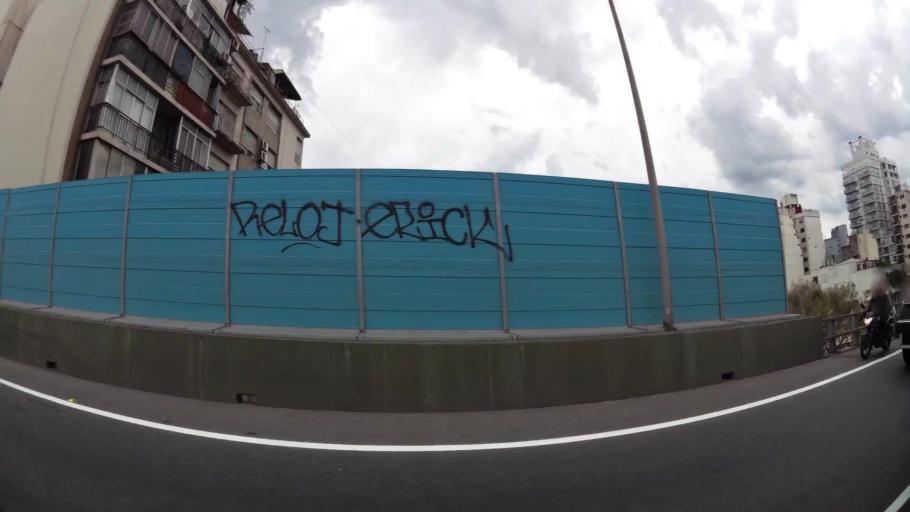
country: AR
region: Buenos Aires F.D.
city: Buenos Aires
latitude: -34.6228
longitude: -58.3727
